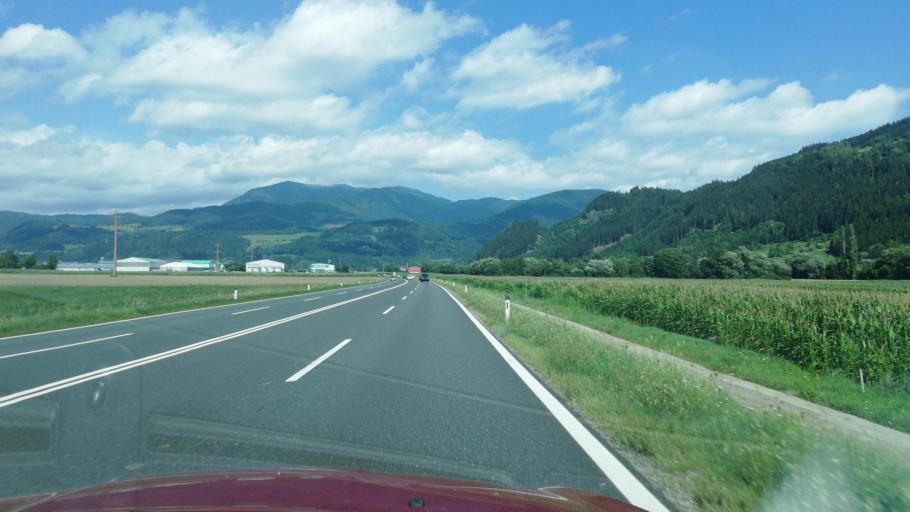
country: AT
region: Carinthia
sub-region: Politischer Bezirk Sankt Veit an der Glan
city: Friesach
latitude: 46.9573
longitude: 14.4107
